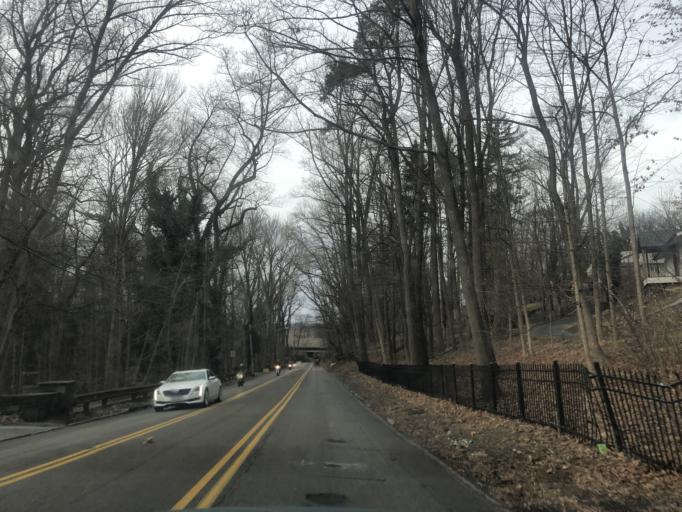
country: US
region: Pennsylvania
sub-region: Delaware County
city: Radnor
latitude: 40.0525
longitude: -75.3361
